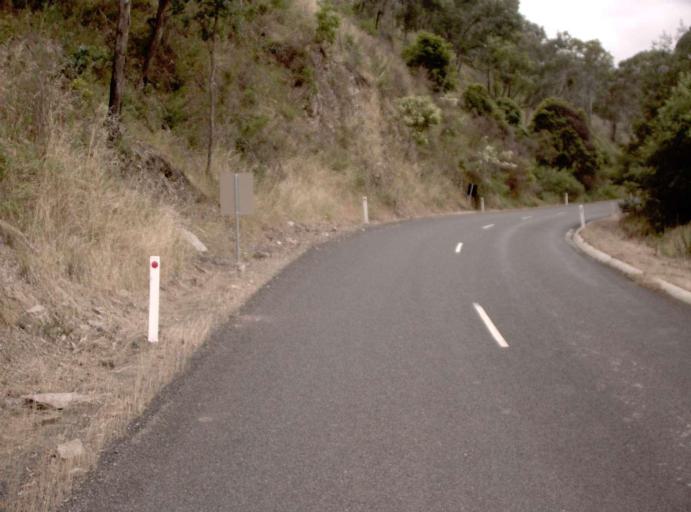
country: AU
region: Victoria
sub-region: Wellington
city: Heyfield
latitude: -37.8003
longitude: 146.6720
